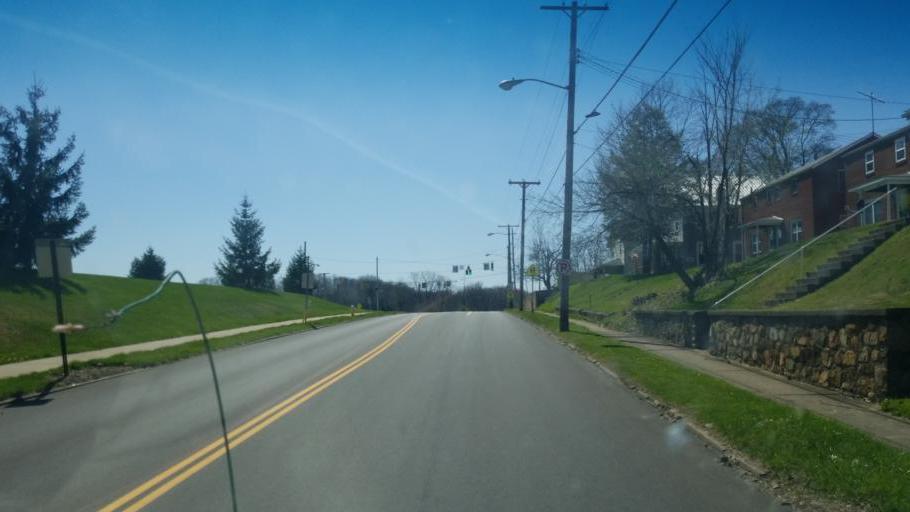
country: US
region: Ohio
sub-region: Richland County
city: Mansfield
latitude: 40.7647
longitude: -82.5410
